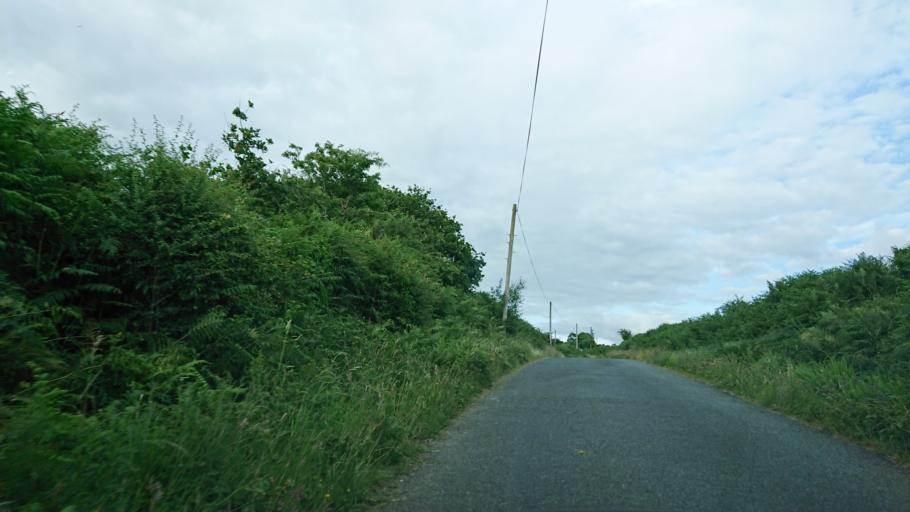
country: IE
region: Munster
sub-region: Waterford
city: Tra Mhor
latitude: 52.2055
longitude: -7.2176
